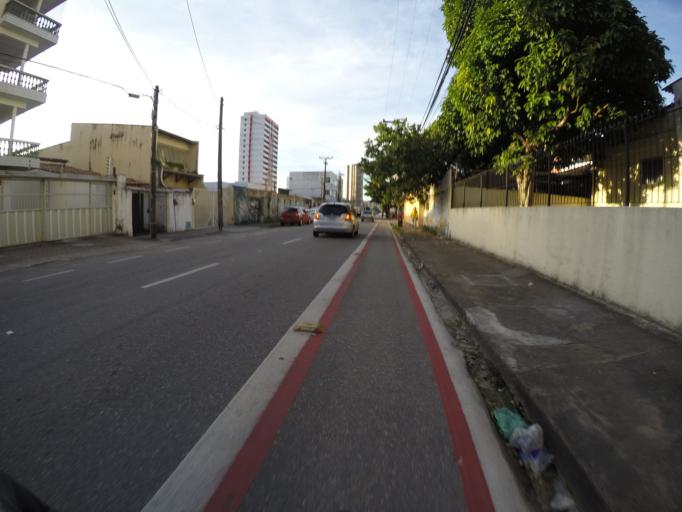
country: BR
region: Ceara
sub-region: Fortaleza
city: Fortaleza
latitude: -3.7429
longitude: -38.5140
